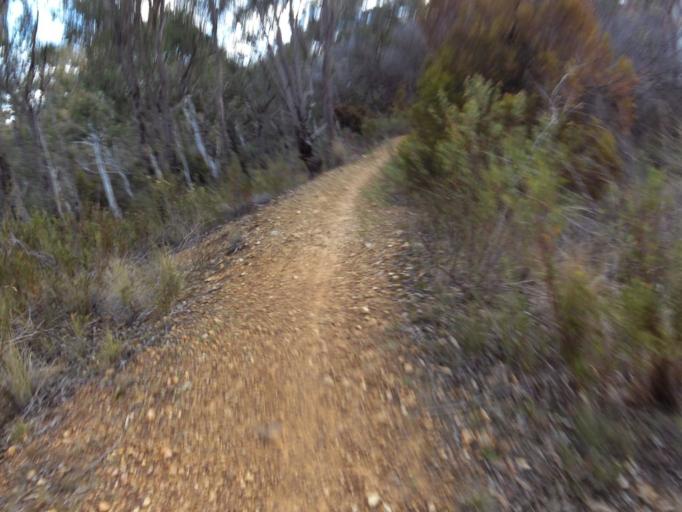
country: AU
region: Australian Capital Territory
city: Acton
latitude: -35.2631
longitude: 149.1117
